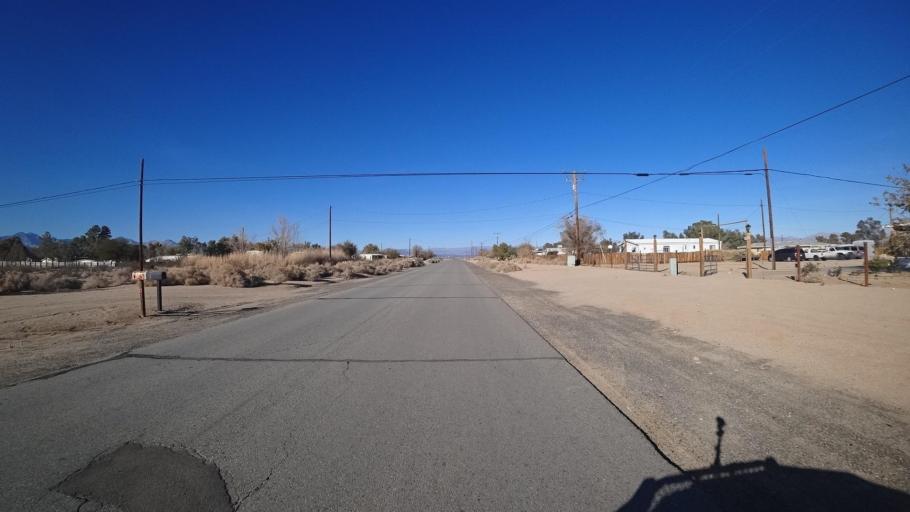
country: US
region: California
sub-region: Kern County
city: China Lake Acres
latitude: 35.6479
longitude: -117.7587
